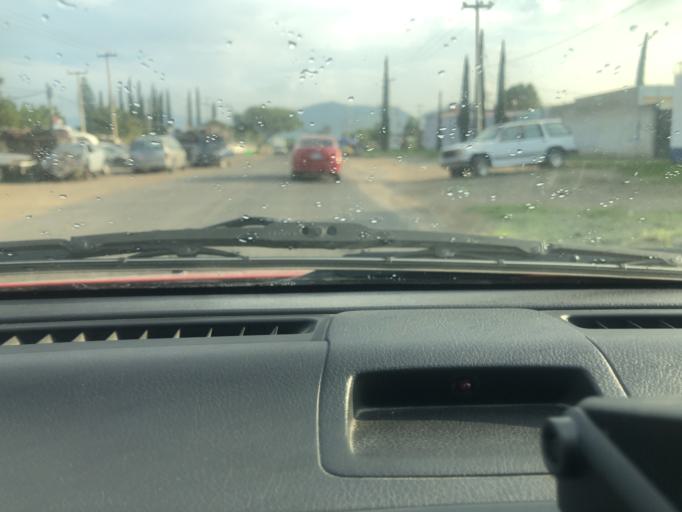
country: MX
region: Jalisco
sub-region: San Pedro Tlaquepaque
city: Santa Anita
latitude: 20.5538
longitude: -103.4188
